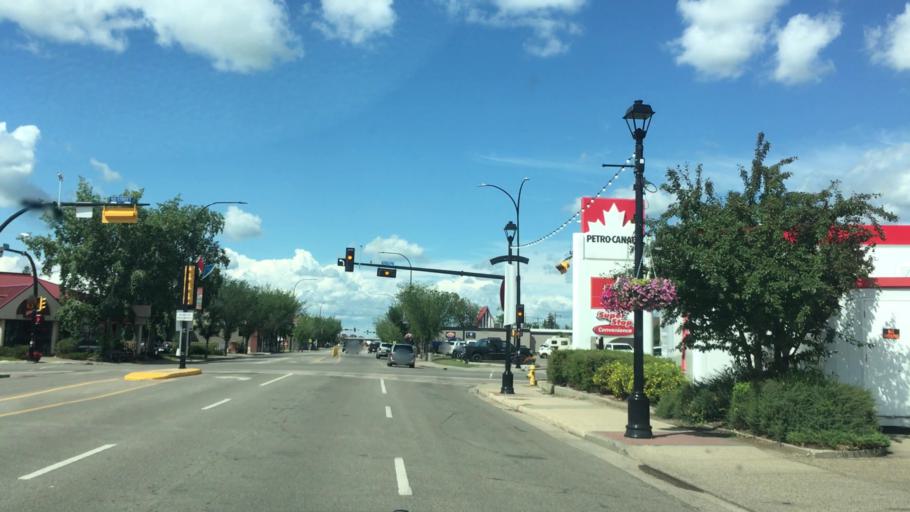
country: CA
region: Alberta
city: Leduc
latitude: 53.2648
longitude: -113.5518
